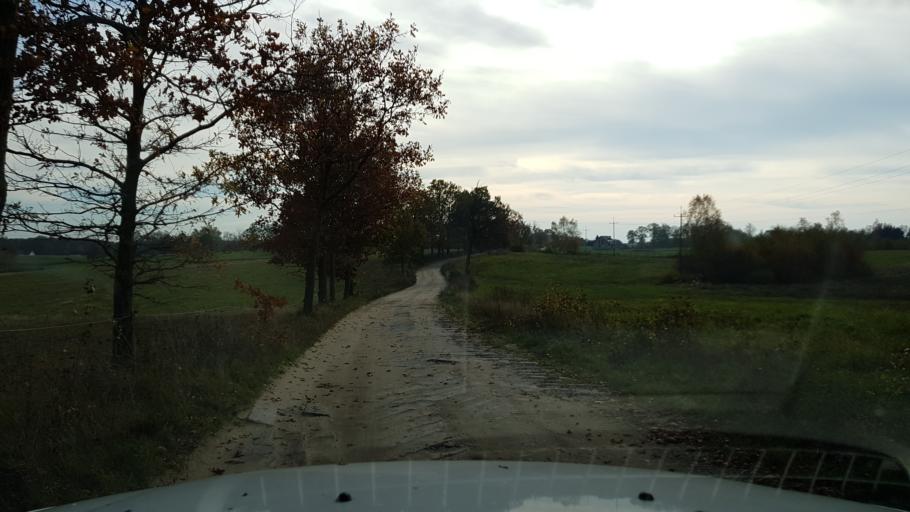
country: PL
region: West Pomeranian Voivodeship
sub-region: Powiat swidwinski
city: Polczyn-Zdroj
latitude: 53.7499
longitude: 16.0334
